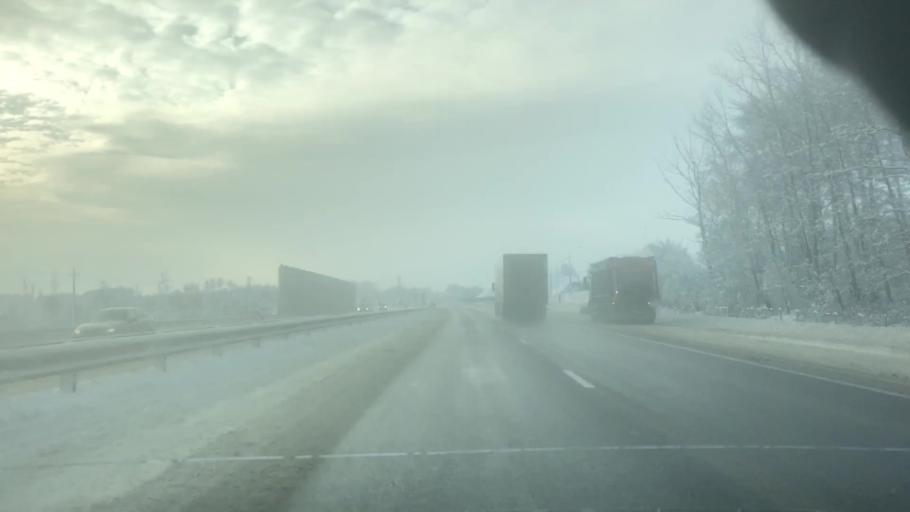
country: RU
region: Tula
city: Venev
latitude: 54.3943
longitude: 38.1562
